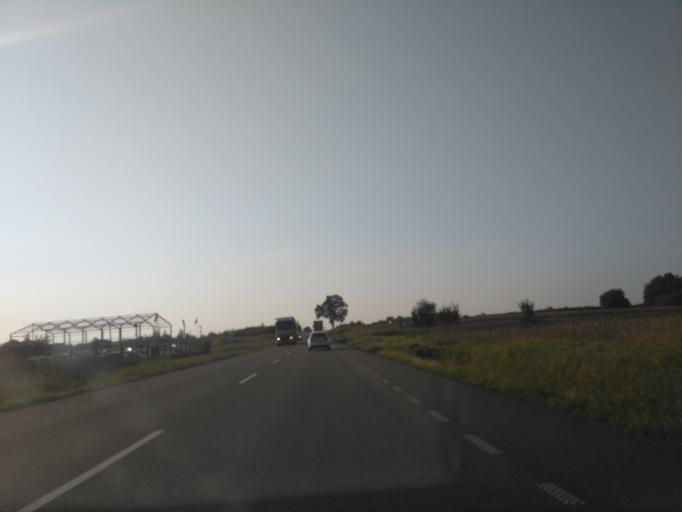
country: PL
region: Lublin Voivodeship
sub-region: Powiat janowski
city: Modliborzyce
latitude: 50.7433
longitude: 22.3441
